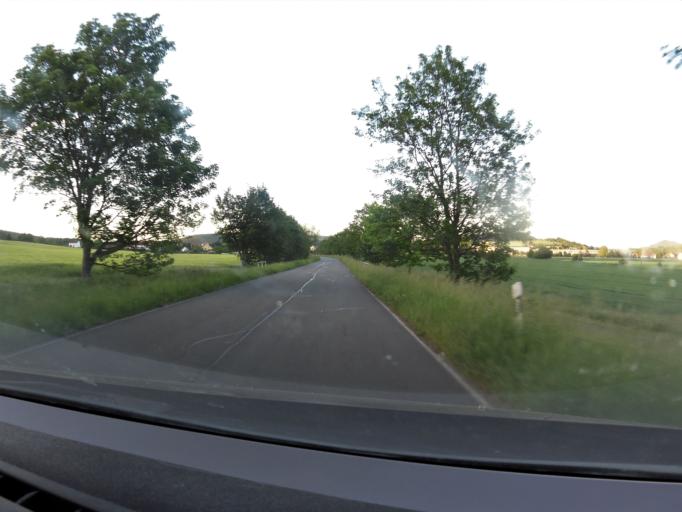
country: DE
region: Thuringia
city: Vacha
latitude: 50.8352
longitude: 10.0329
